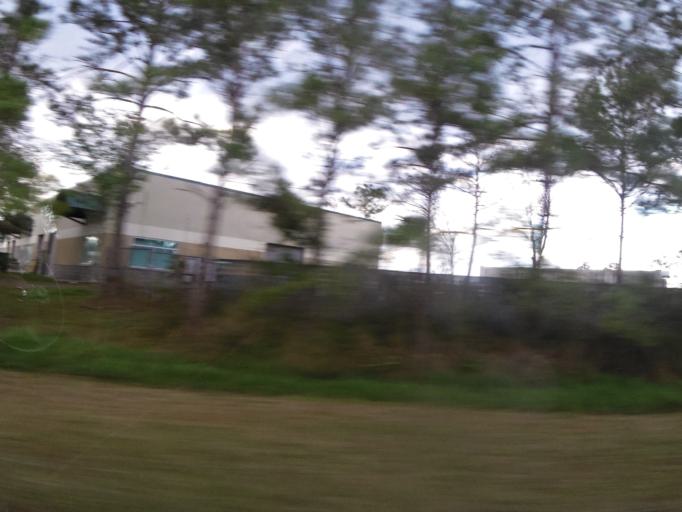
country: US
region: Florida
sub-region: Saint Johns County
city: Fruit Cove
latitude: 30.1845
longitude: -81.5738
